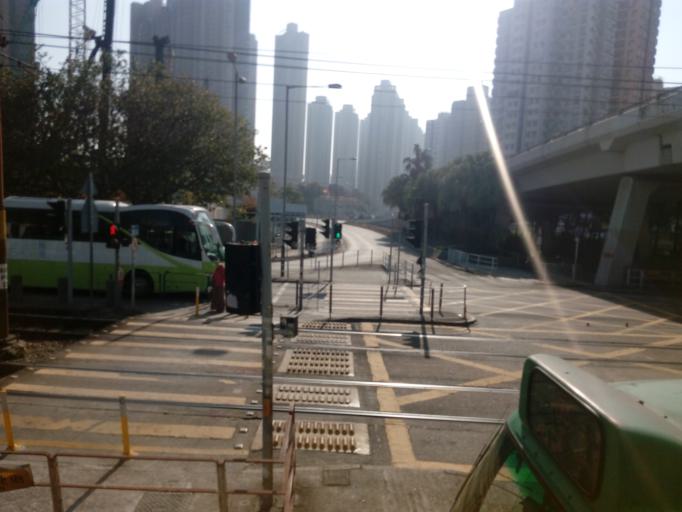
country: HK
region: Yuen Long
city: Yuen Long Kau Hui
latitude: 22.4450
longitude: 114.0327
